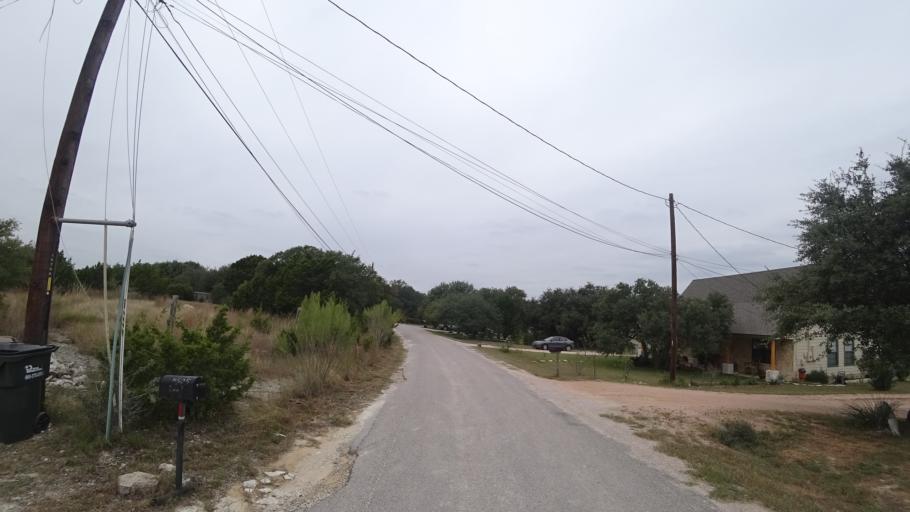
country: US
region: Texas
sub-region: Travis County
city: Lakeway
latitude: 30.3686
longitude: -97.9334
